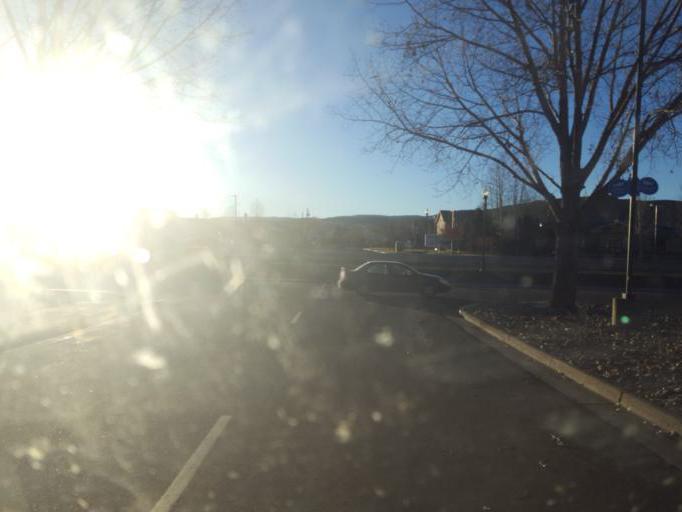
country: US
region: Colorado
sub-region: Gunnison County
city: Gunnison
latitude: 38.5543
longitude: -106.9260
